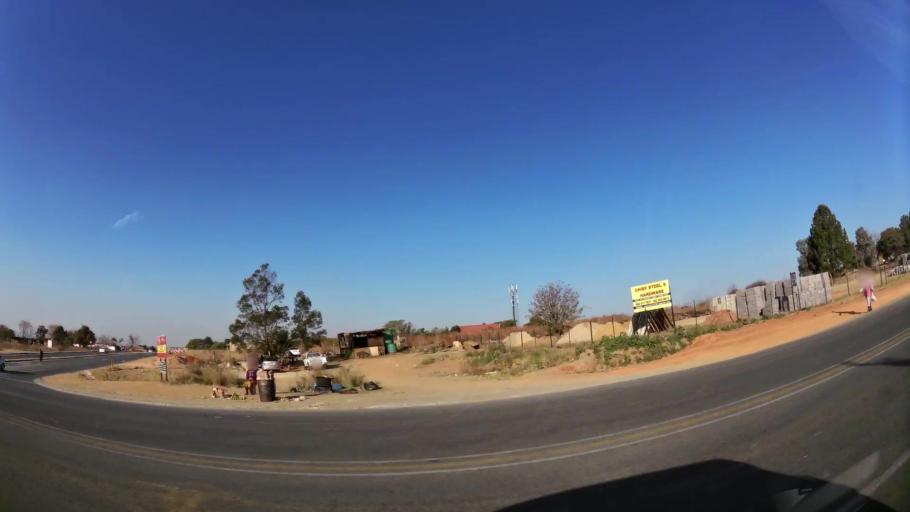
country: ZA
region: Gauteng
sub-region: West Rand District Municipality
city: Muldersdriseloop
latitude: -26.0436
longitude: 27.9082
